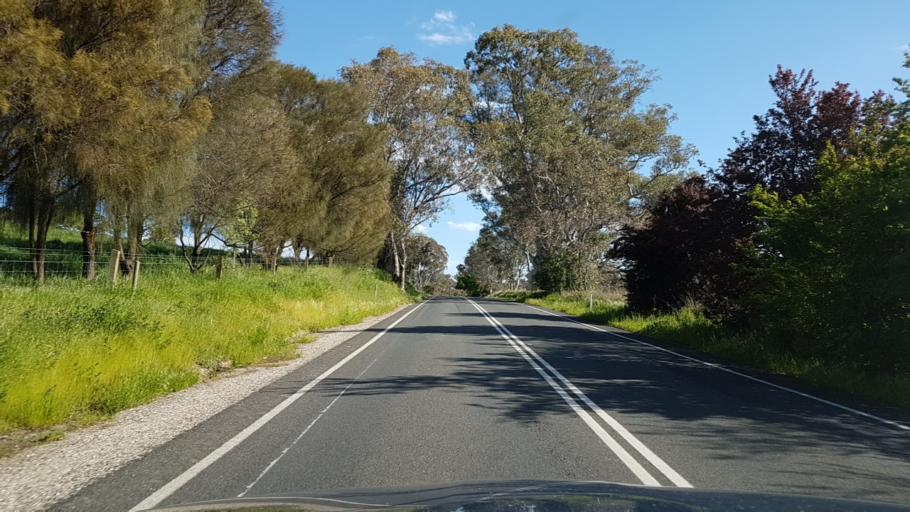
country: AU
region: South Australia
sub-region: Adelaide Hills
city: Gumeracha
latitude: -34.8428
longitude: 138.8936
